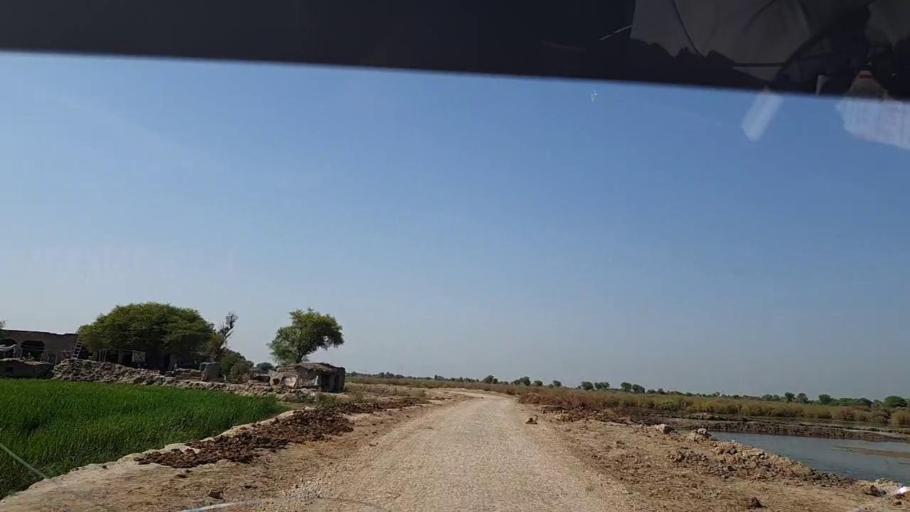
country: PK
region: Sindh
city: Tangwani
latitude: 28.3272
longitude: 69.0794
